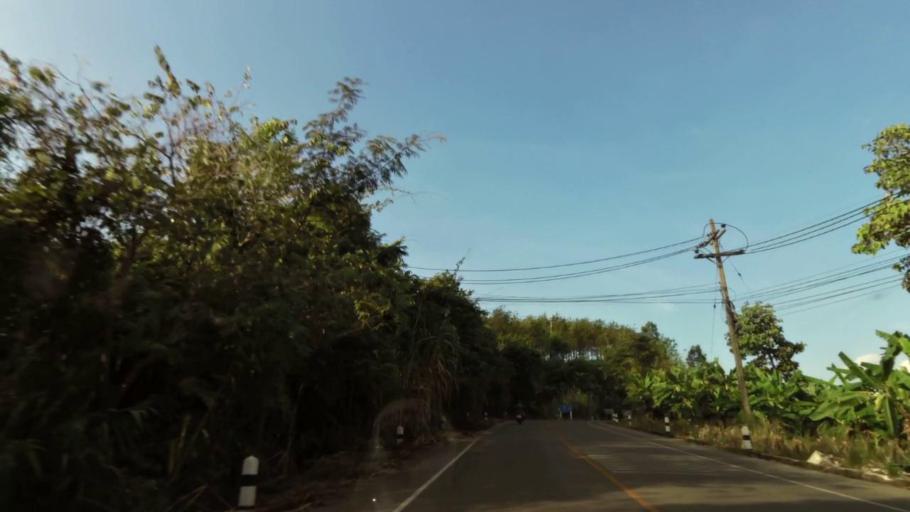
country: TH
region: Chiang Rai
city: Khun Tan
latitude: 19.8522
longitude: 100.3806
